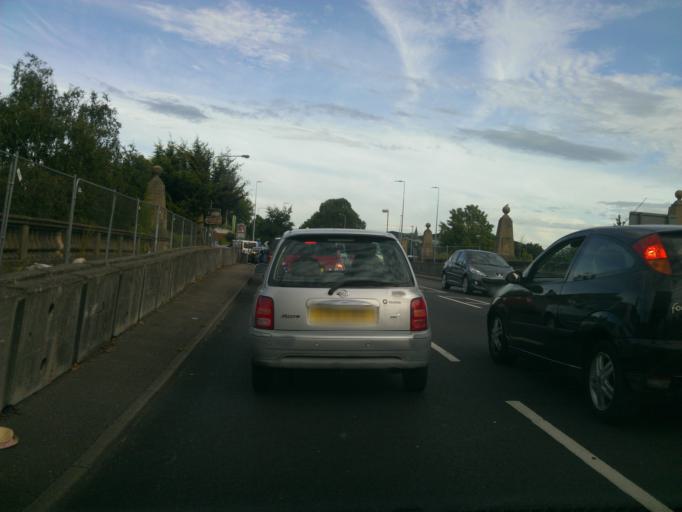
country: GB
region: England
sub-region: Essex
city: Colchester
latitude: 51.8935
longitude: 0.9166
